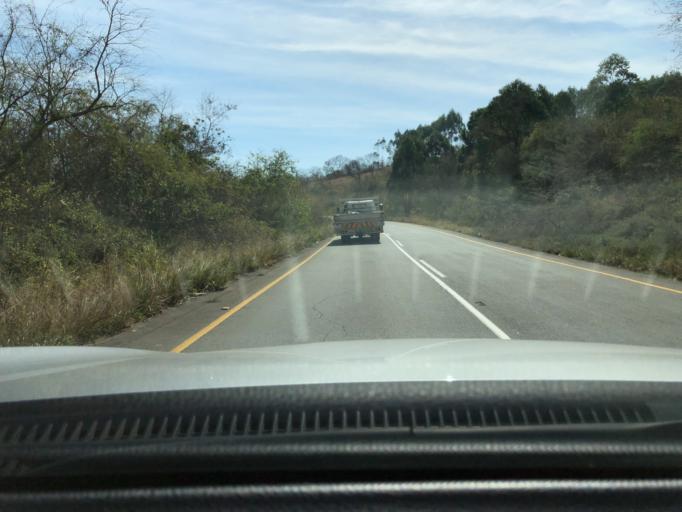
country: ZA
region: KwaZulu-Natal
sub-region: uMgungundlovu District Municipality
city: Richmond
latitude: -29.9588
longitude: 30.2552
